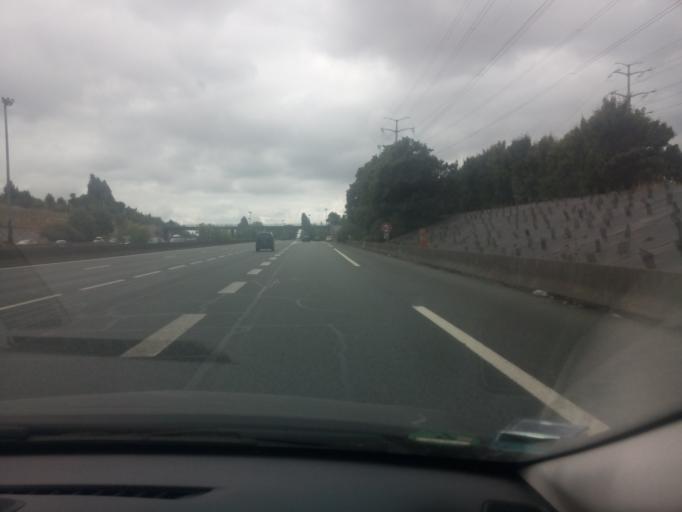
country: FR
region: Ile-de-France
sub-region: Departement de l'Essonne
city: Wissous
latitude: 48.7432
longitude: 2.3222
